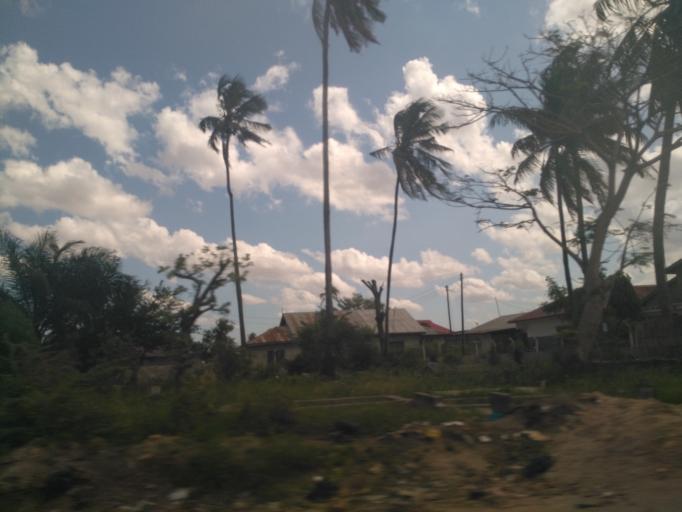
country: TZ
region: Dar es Salaam
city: Dar es Salaam
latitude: -6.8716
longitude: 39.2350
